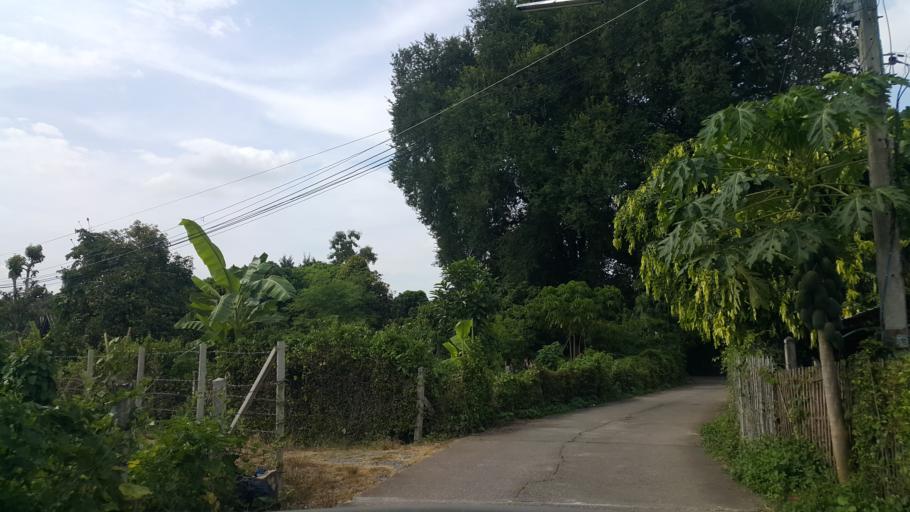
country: TH
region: Chiang Mai
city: San Sai
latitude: 18.9073
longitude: 99.1288
